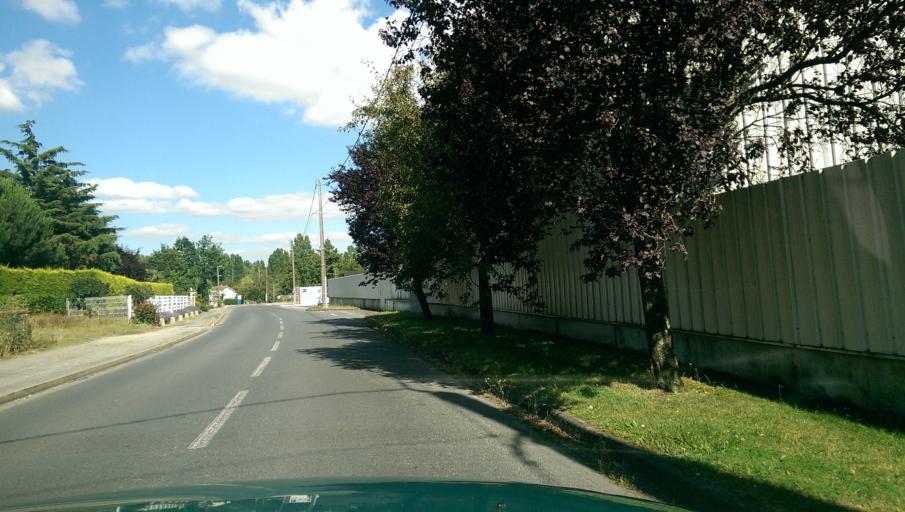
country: FR
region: Pays de la Loire
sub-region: Departement de la Loire-Atlantique
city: Lege
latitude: 46.8892
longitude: -1.5923
